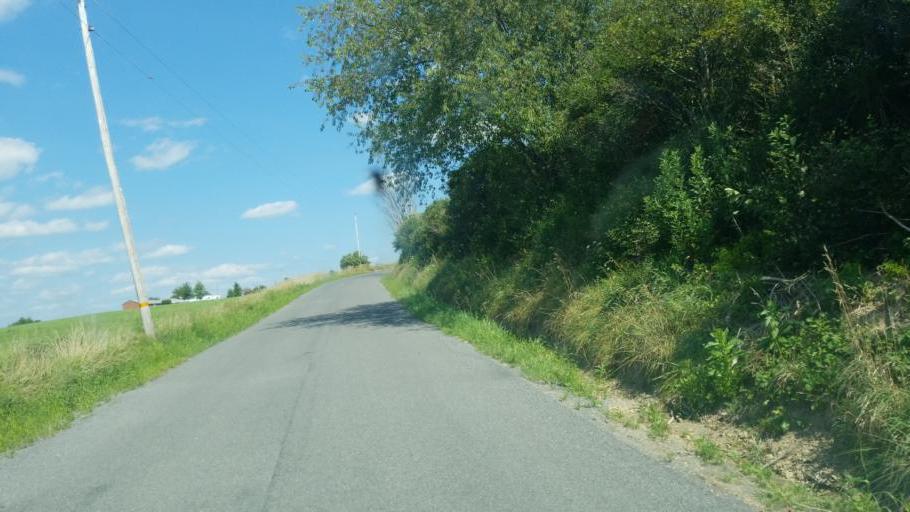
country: US
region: Pennsylvania
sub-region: Clarion County
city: Knox
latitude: 41.0954
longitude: -79.5173
